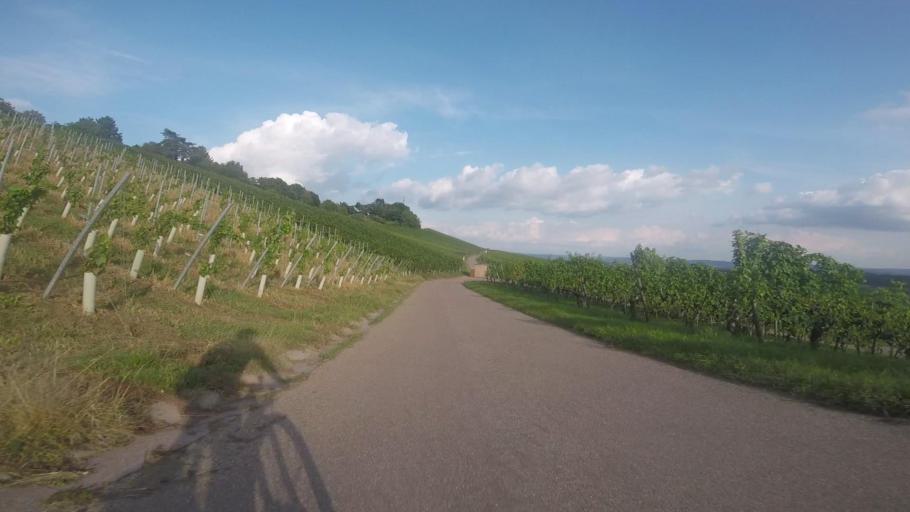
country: DE
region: Baden-Wuerttemberg
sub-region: Regierungsbezirk Stuttgart
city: Aspach
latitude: 49.0002
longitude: 9.3694
